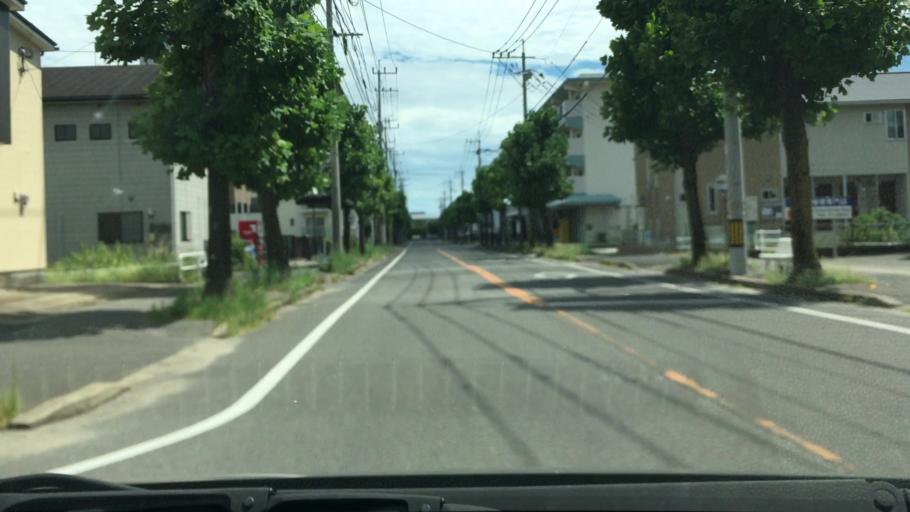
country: JP
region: Saga Prefecture
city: Saga-shi
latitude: 33.2686
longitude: 130.2871
